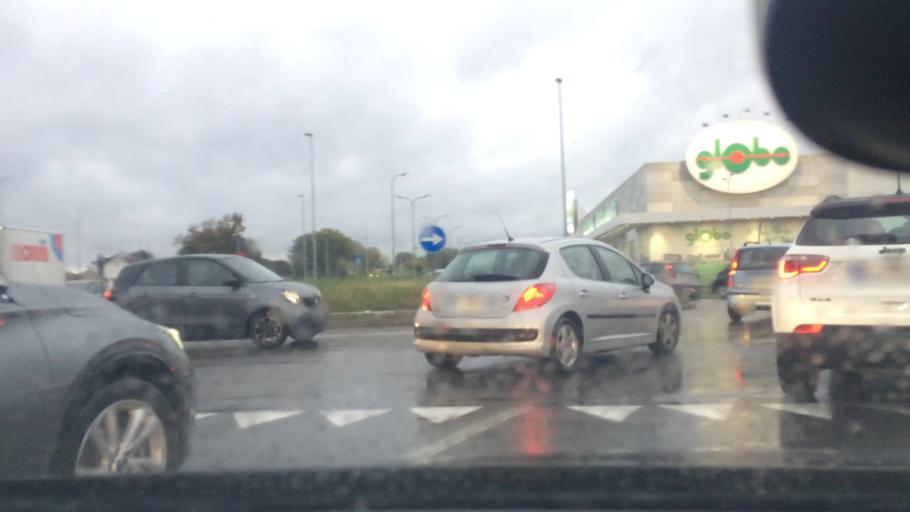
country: IT
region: Lombardy
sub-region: Citta metropolitana di Milano
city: Pogliano Milanese
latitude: 45.5429
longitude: 9.0107
